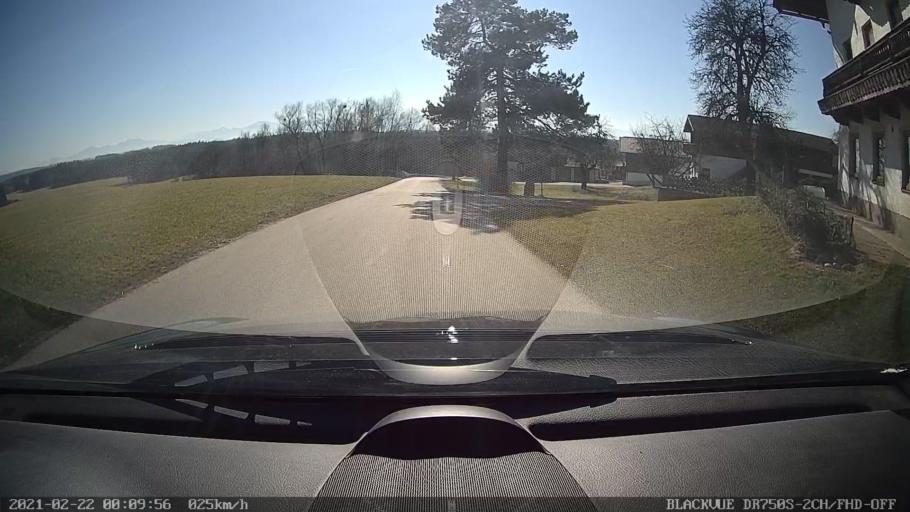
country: DE
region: Bavaria
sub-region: Upper Bavaria
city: Griesstatt
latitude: 47.9770
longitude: 12.1973
